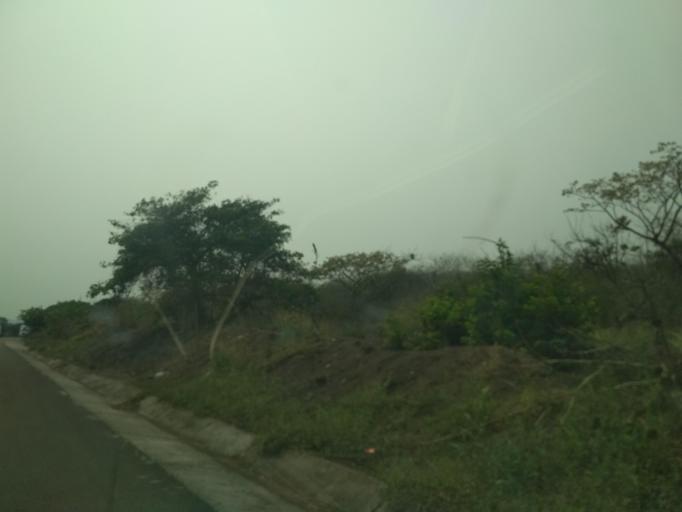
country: MX
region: Veracruz
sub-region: Veracruz
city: Delfino Victoria (Santa Fe)
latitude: 19.2131
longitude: -96.3134
